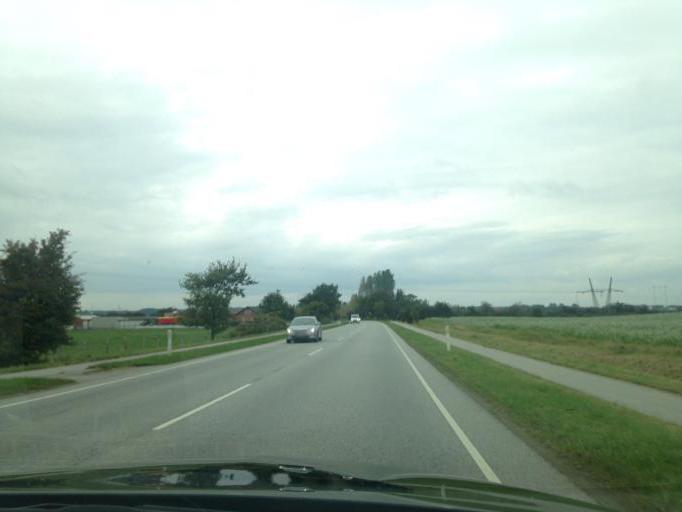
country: DK
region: South Denmark
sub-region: Kolding Kommune
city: Christiansfeld
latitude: 55.3406
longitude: 9.4881
